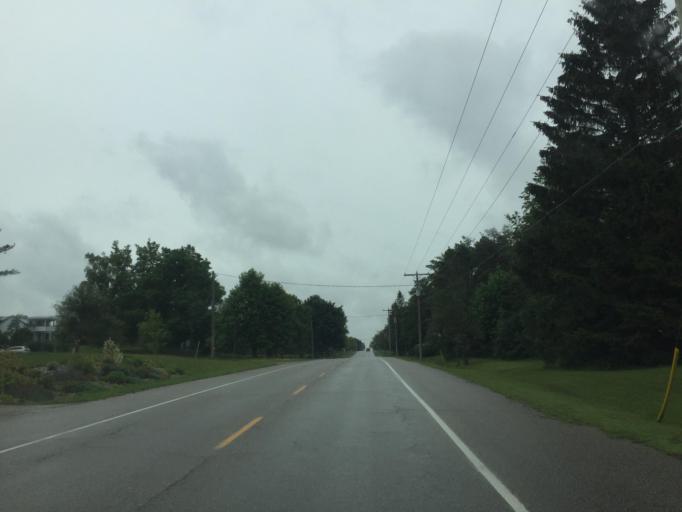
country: CA
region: Ontario
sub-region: Wellington County
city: Guelph
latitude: 43.4489
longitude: -80.2300
